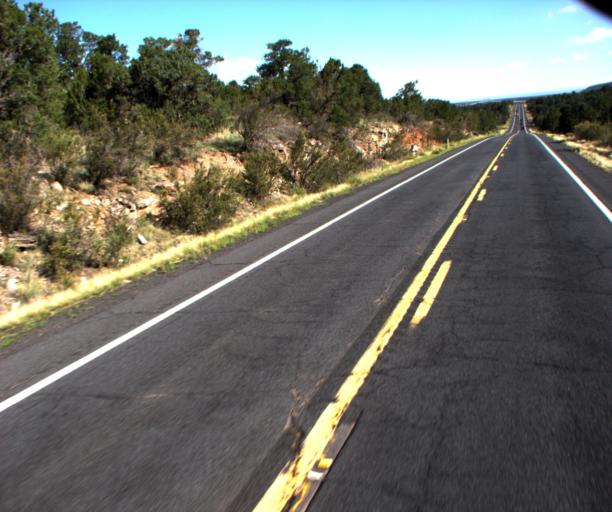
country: US
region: Arizona
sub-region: Coconino County
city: Williams
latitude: 35.4226
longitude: -112.1706
